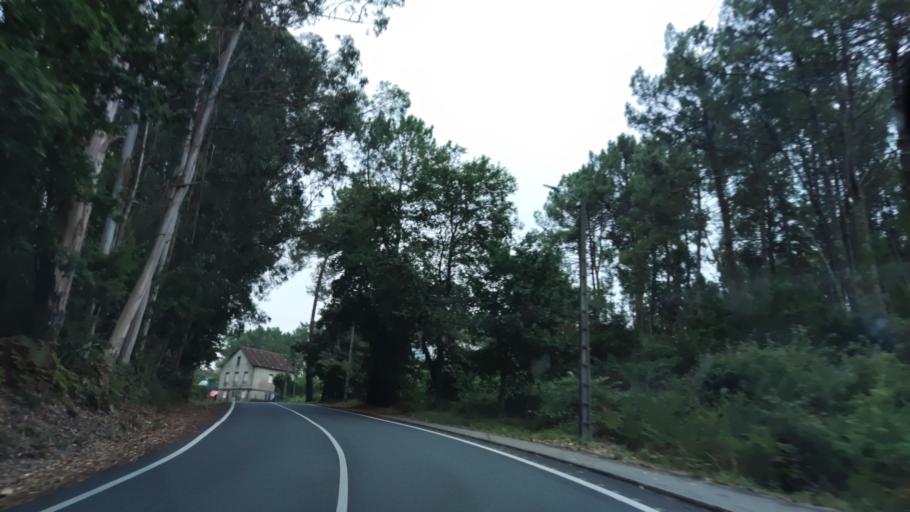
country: ES
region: Galicia
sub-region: Provincia de Pontevedra
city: Catoira
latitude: 42.6831
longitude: -8.7345
